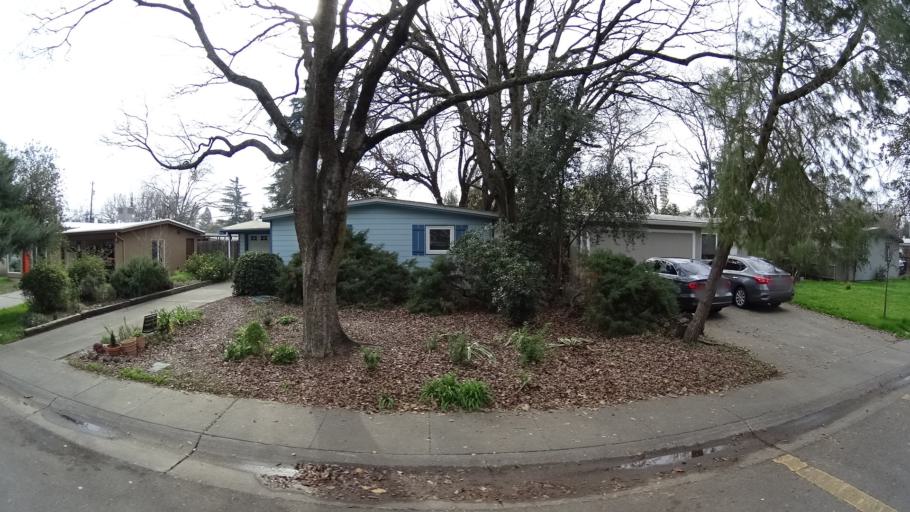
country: US
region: California
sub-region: Yolo County
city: Davis
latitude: 38.5509
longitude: -121.7332
